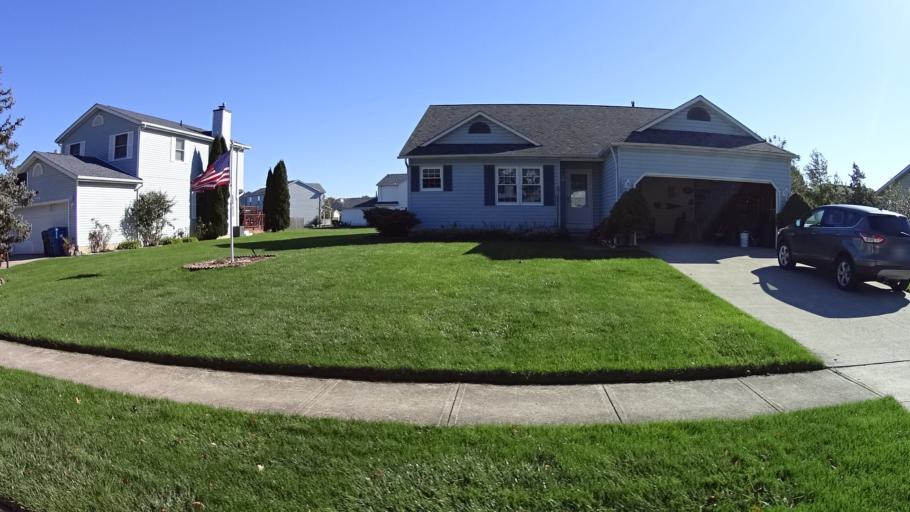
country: US
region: Ohio
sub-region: Lorain County
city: Amherst
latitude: 41.4220
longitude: -82.2193
